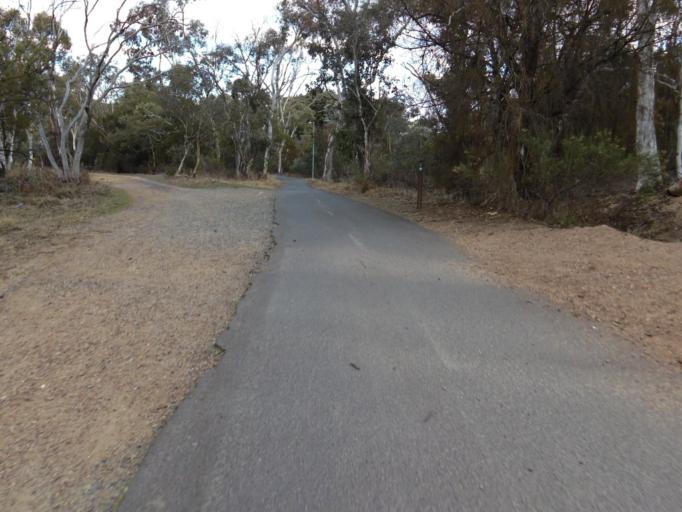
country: AU
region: Australian Capital Territory
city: Acton
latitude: -35.2547
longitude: 149.1090
